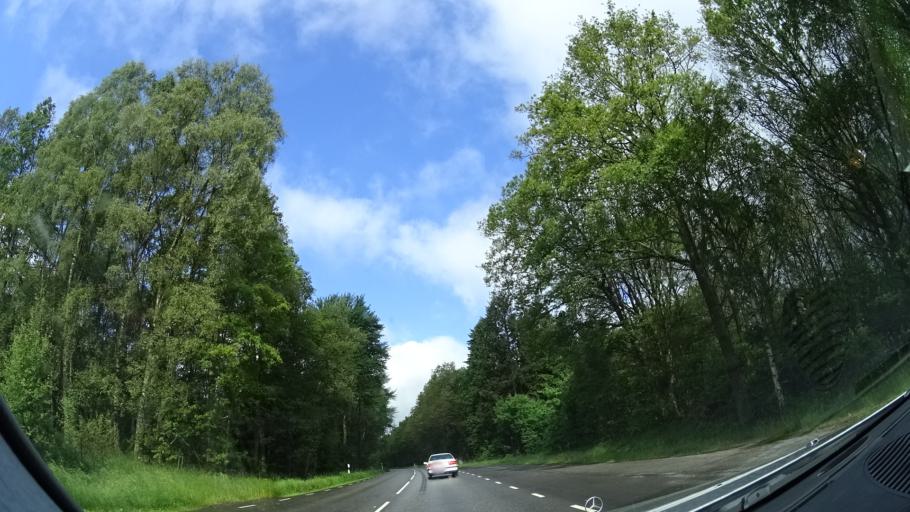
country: SE
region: Skane
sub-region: Eslovs Kommun
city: Stehag
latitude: 55.9436
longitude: 13.4080
